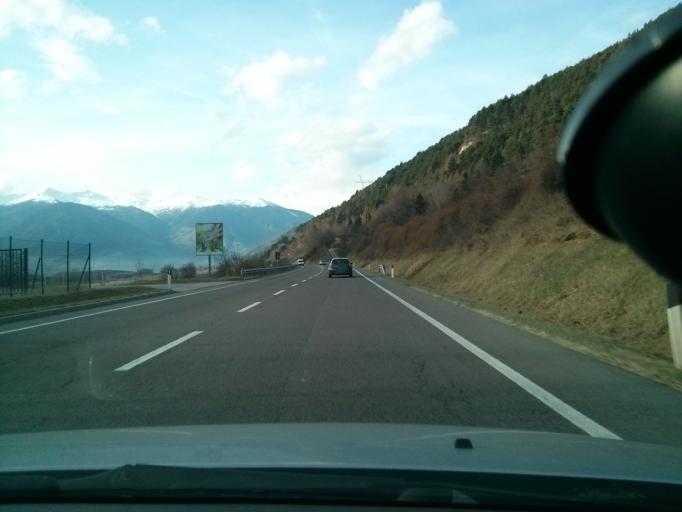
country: IT
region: Trentino-Alto Adige
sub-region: Bolzano
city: Lasa
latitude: 46.6274
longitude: 10.6802
